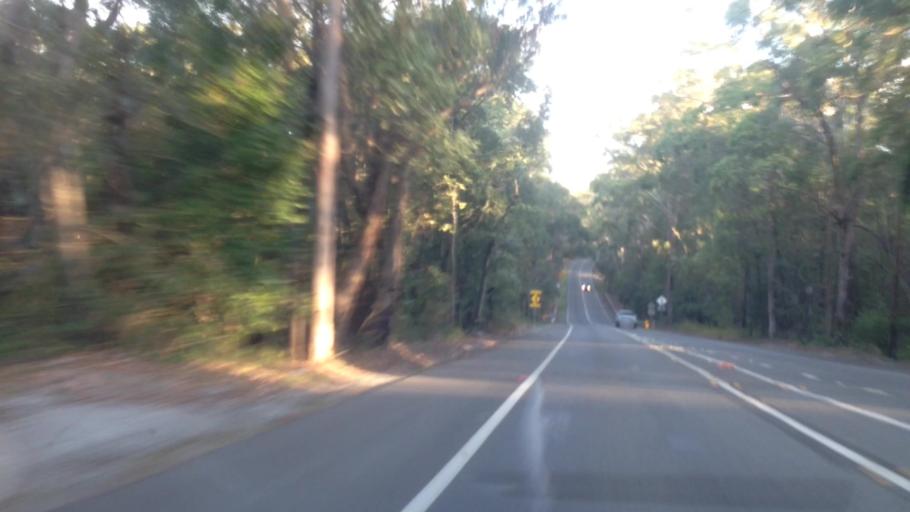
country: AU
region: New South Wales
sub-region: Lake Macquarie Shire
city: Cooranbong
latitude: -32.9752
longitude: 151.4822
